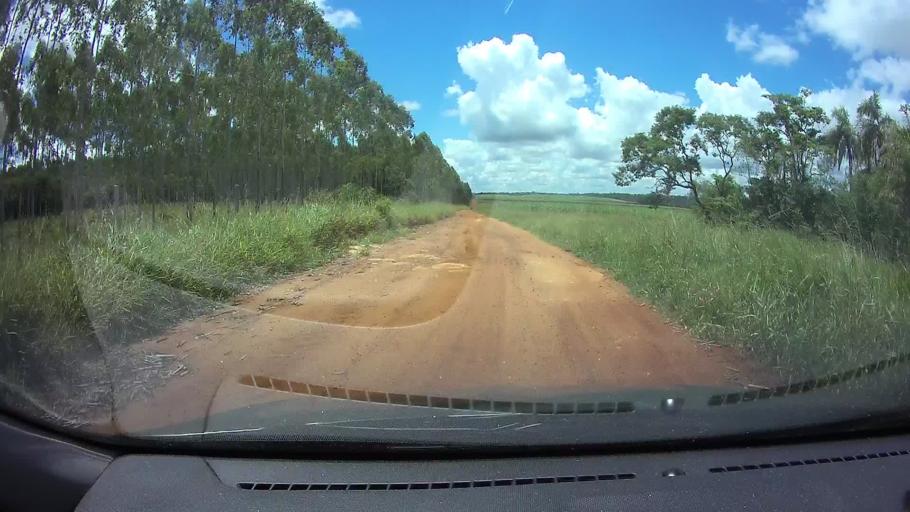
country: PY
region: Paraguari
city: La Colmena
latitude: -25.9647
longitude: -56.7326
